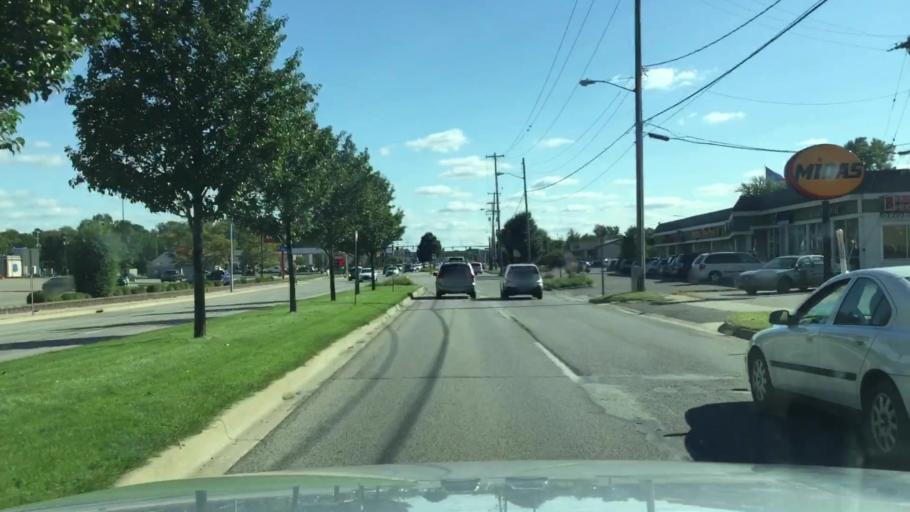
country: US
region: Michigan
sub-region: Kalamazoo County
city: Portage
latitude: 42.2430
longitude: -85.5896
